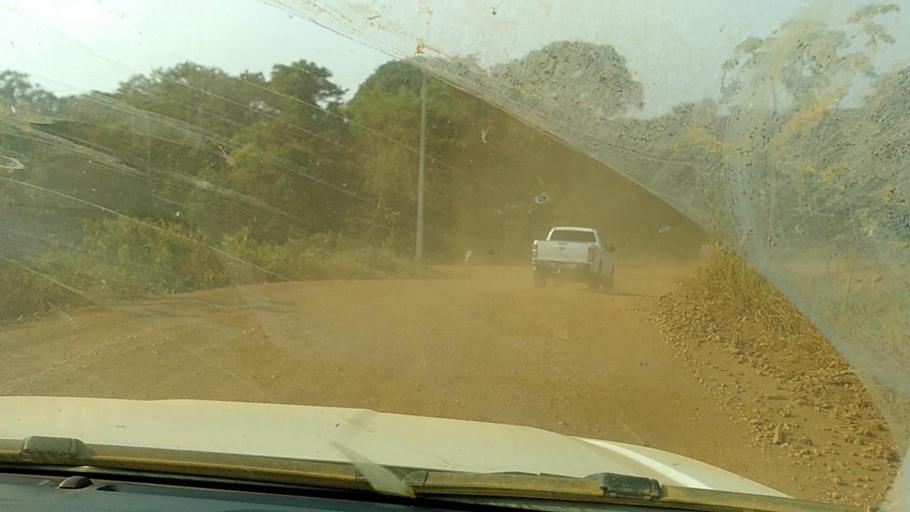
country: BR
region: Rondonia
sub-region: Porto Velho
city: Porto Velho
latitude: -8.7583
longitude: -63.9610
